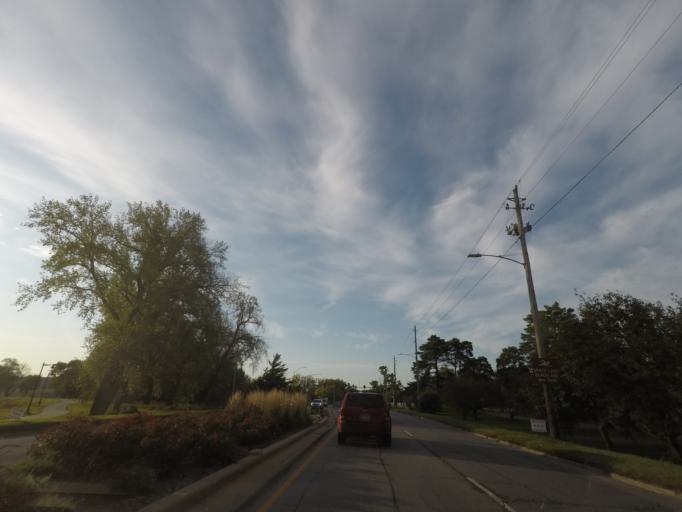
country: US
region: Iowa
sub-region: Polk County
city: Des Moines
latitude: 41.5747
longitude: -93.6450
